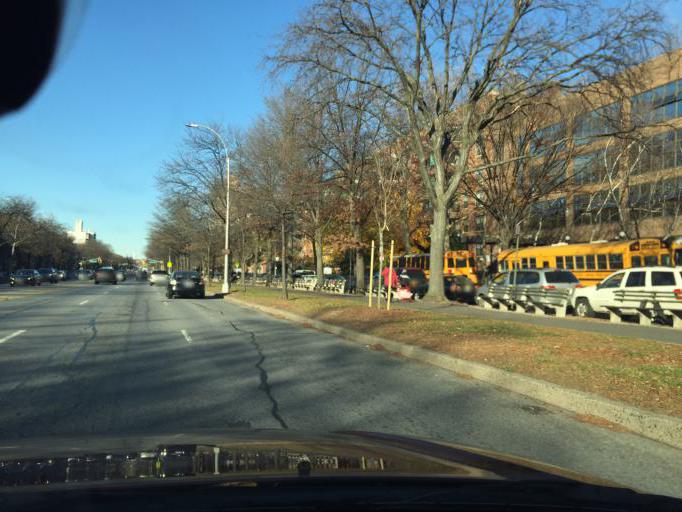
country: US
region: New York
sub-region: Kings County
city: Brooklyn
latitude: 40.6344
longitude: -73.9724
